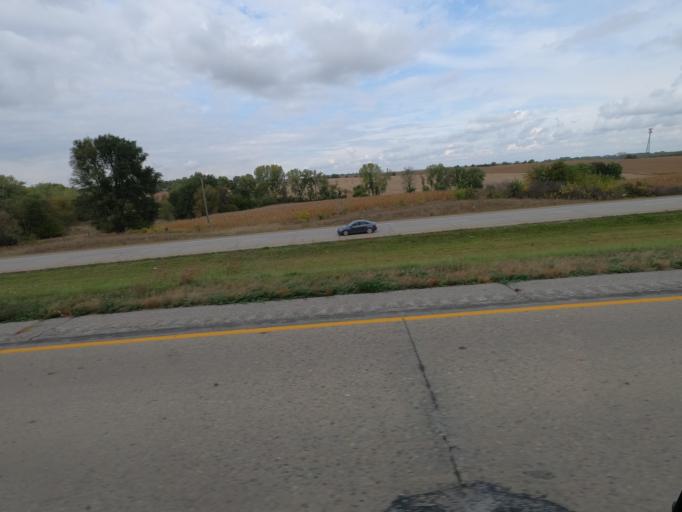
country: US
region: Iowa
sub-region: Polk County
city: Mitchellville
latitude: 41.6005
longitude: -93.3837
